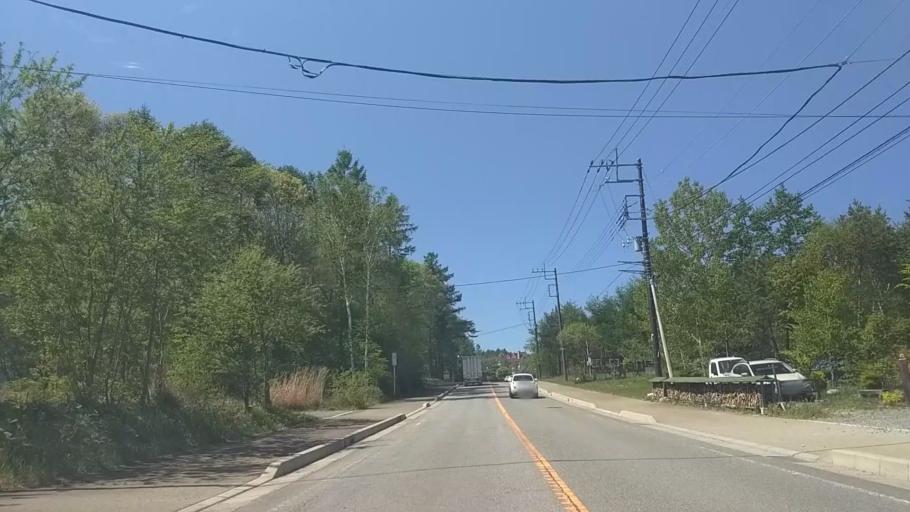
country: JP
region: Yamanashi
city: Nirasaki
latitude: 35.9172
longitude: 138.4411
